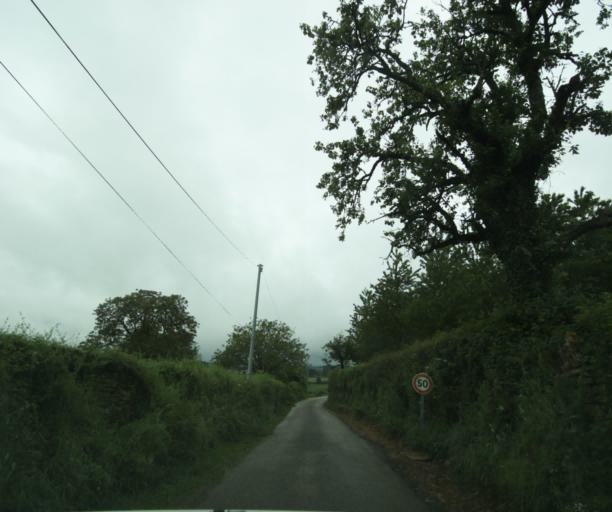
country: FR
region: Bourgogne
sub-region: Departement de Saone-et-Loire
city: Charolles
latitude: 46.3797
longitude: 4.2316
